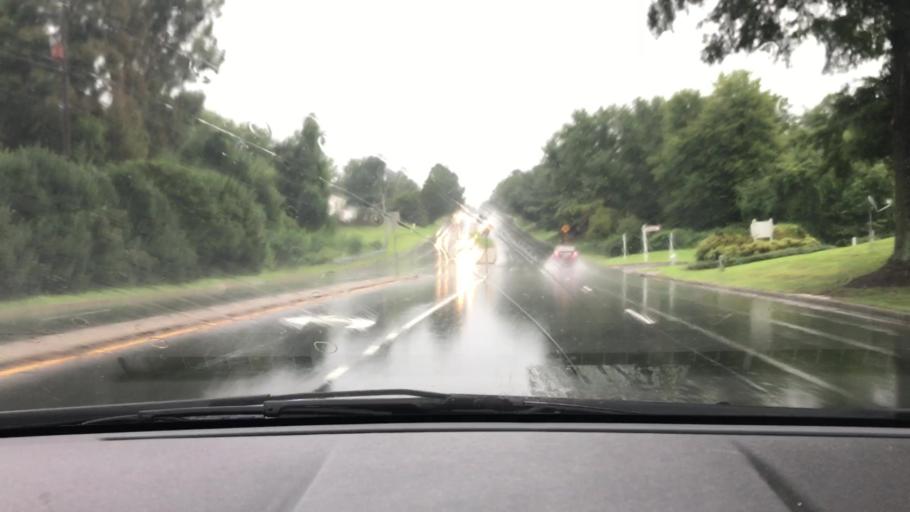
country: US
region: Virginia
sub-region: Henrico County
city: Laurel
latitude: 37.6489
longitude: -77.5573
